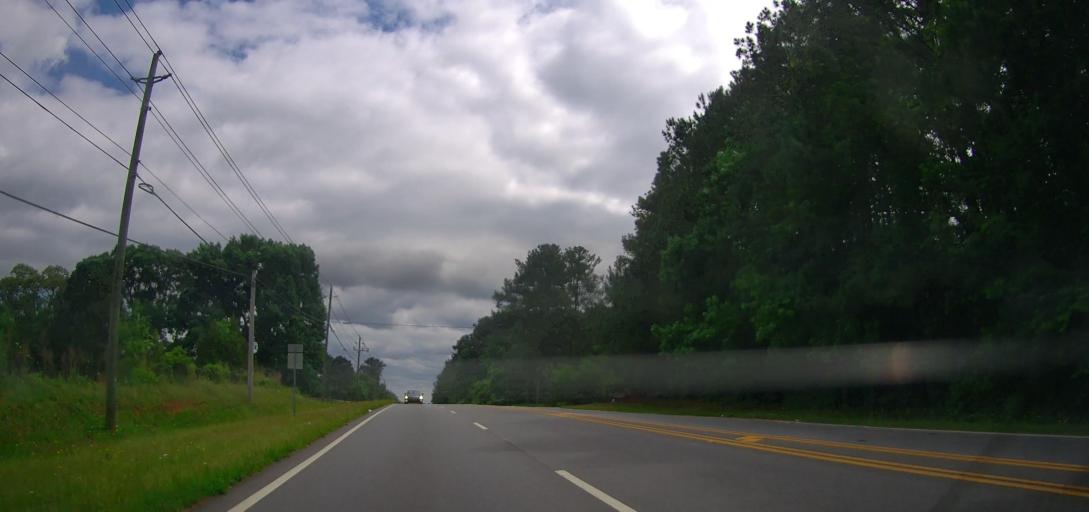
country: US
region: Georgia
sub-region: DeKalb County
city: Pine Mountain
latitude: 33.6120
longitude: -84.0957
